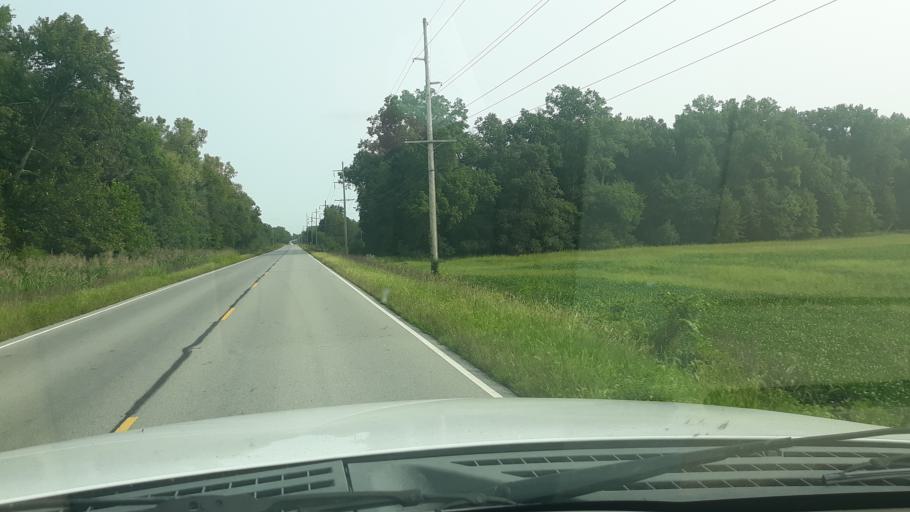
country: US
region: Illinois
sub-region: White County
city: Norris City
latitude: 37.9334
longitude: -88.3463
